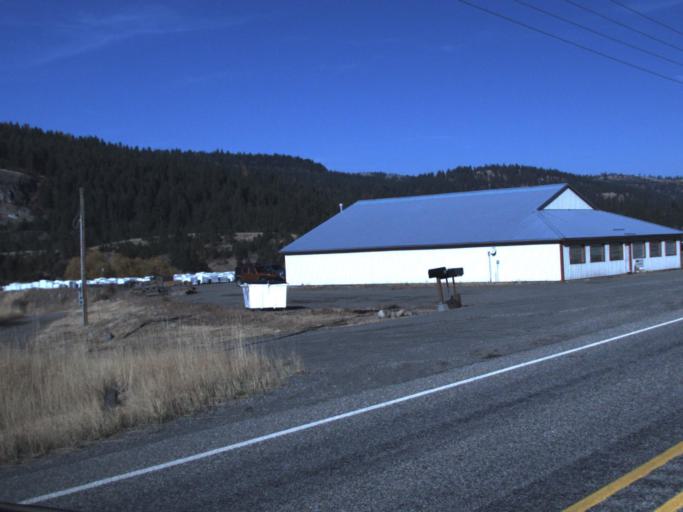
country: US
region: Washington
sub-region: Ferry County
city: Republic
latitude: 48.6868
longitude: -118.6626
